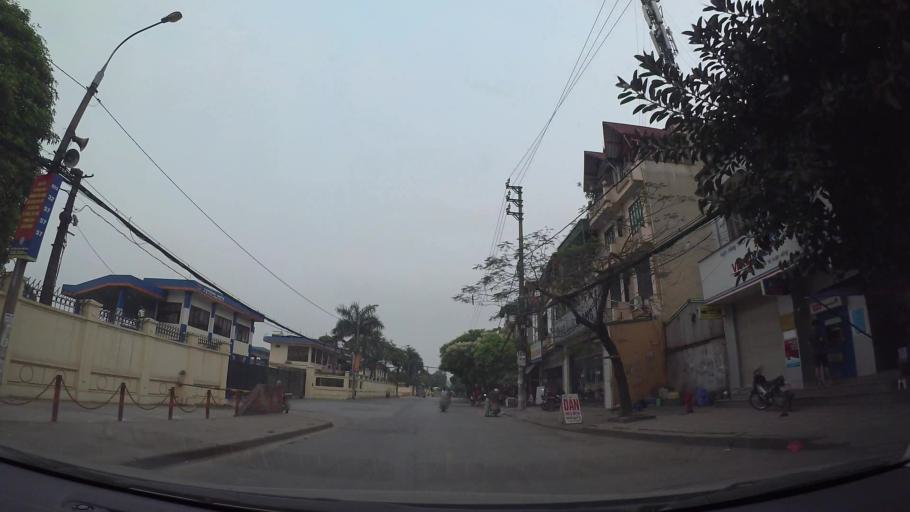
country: VN
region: Ha Noi
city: Hoan Kiem
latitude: 21.0672
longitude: 105.8910
